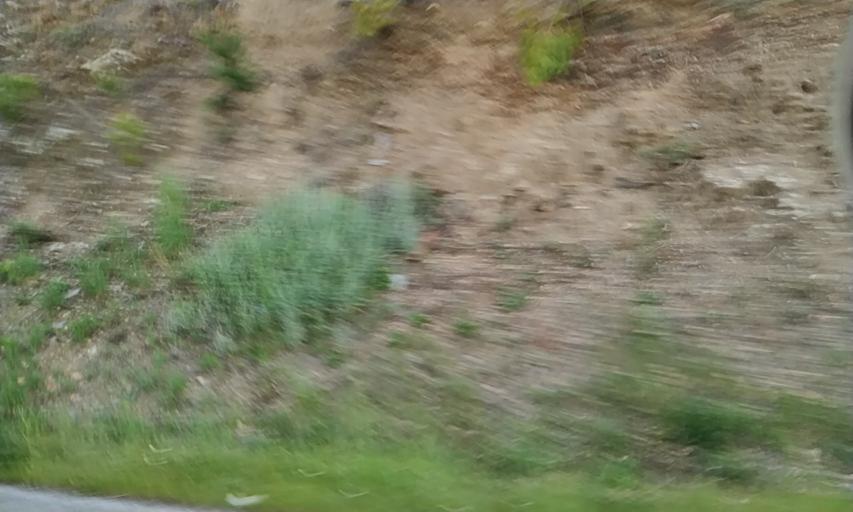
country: PT
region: Portalegre
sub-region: Portalegre
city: Sao Juliao
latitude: 39.3583
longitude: -7.3177
